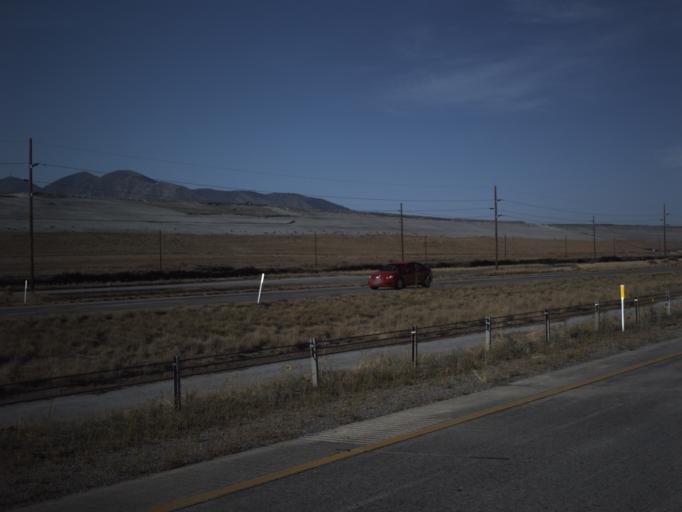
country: US
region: Utah
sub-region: Salt Lake County
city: Magna
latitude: 40.7710
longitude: -112.1093
